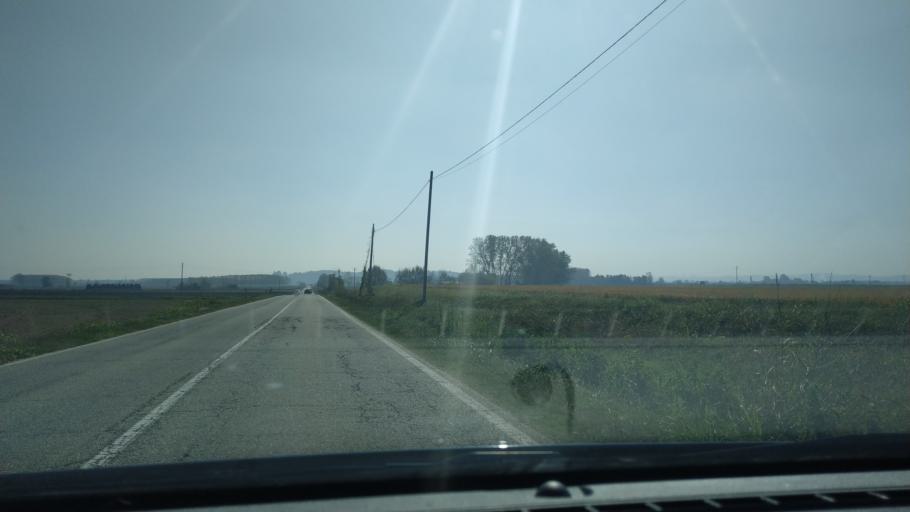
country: IT
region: Piedmont
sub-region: Provincia di Alessandria
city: Ticineto
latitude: 45.0827
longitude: 8.5597
